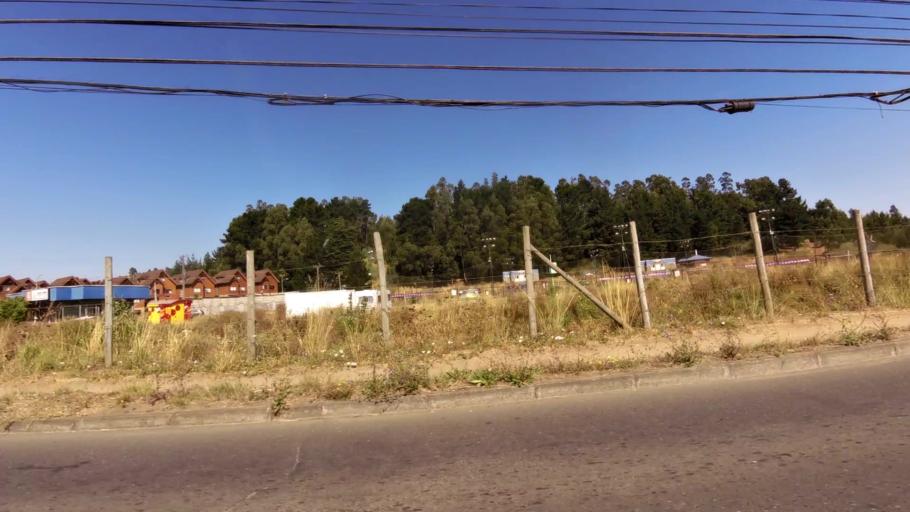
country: CL
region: Biobio
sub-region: Provincia de Concepcion
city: Concepcion
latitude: -36.7826
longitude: -73.0537
